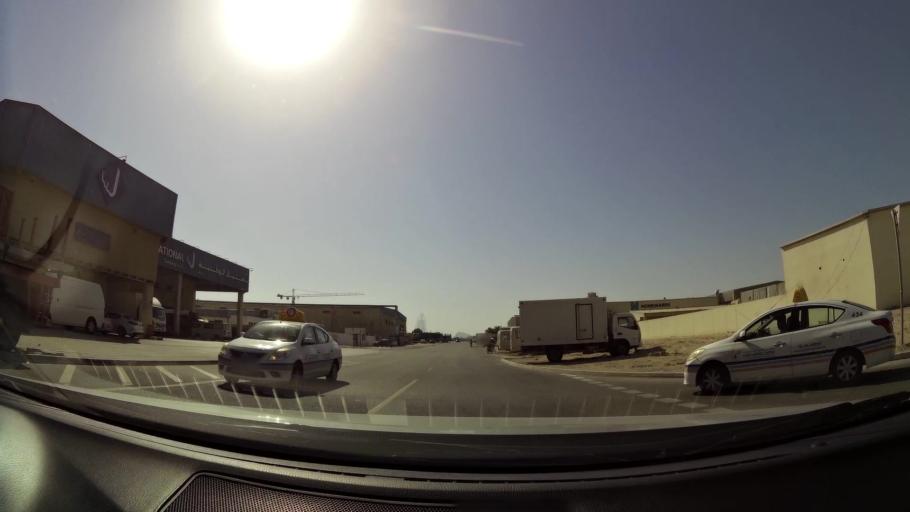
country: AE
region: Dubai
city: Dubai
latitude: 25.1230
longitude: 55.2190
